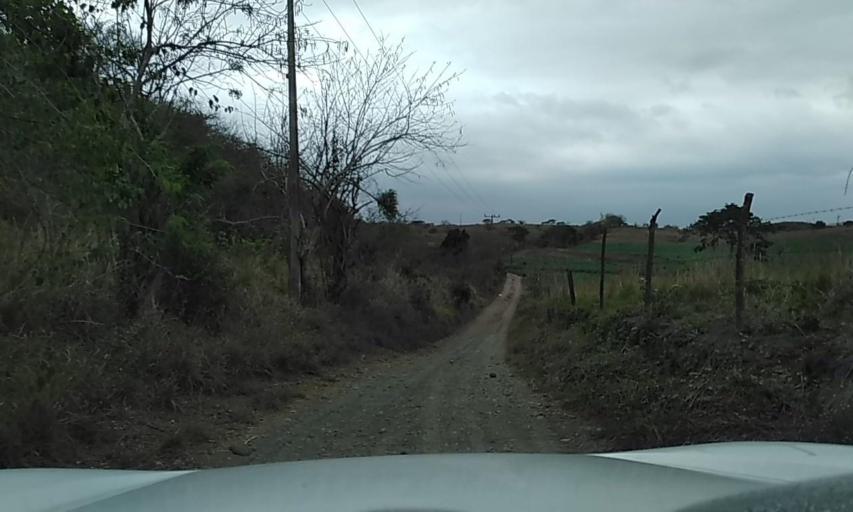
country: MX
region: Veracruz
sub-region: Veracruz
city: Delfino Victoria (Santa Fe)
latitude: 19.2743
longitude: -96.3087
